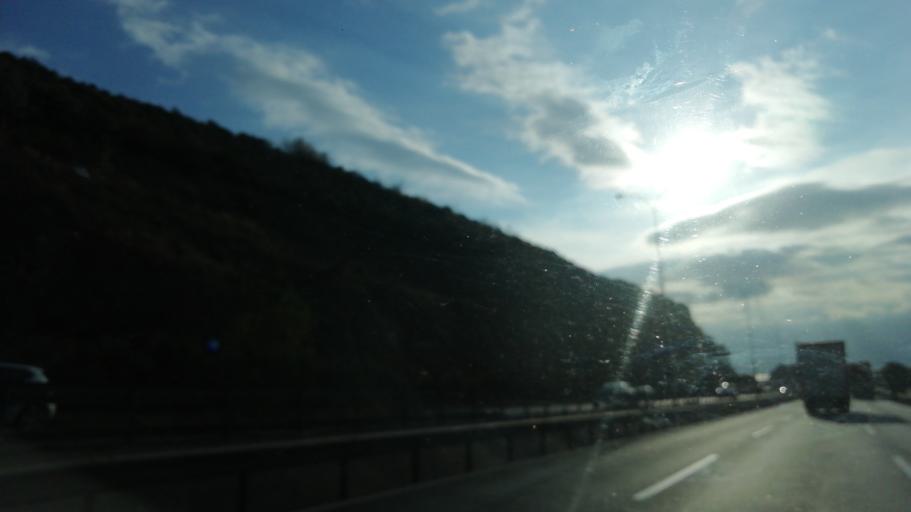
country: TR
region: Kocaeli
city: Hereke
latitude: 40.7815
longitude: 29.6280
